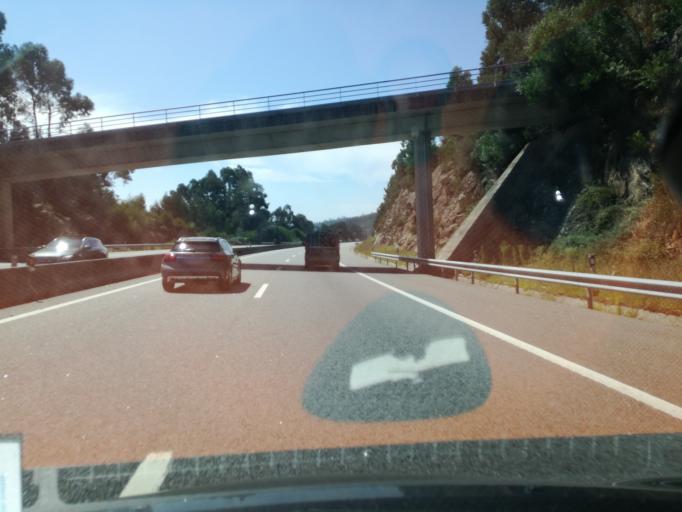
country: PT
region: Viana do Castelo
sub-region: Viana do Castelo
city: Meadela
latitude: 41.7580
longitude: -8.7954
